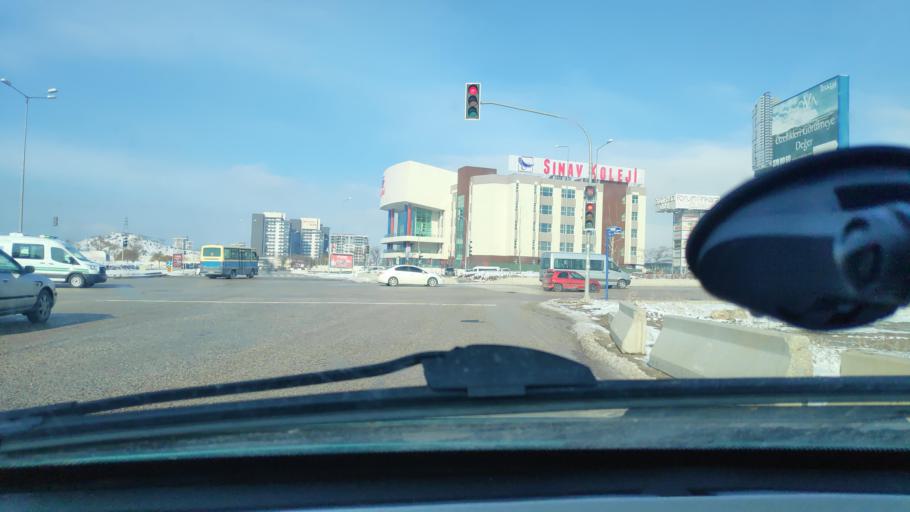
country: TR
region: Ankara
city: Ankara
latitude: 40.0145
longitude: 32.8276
